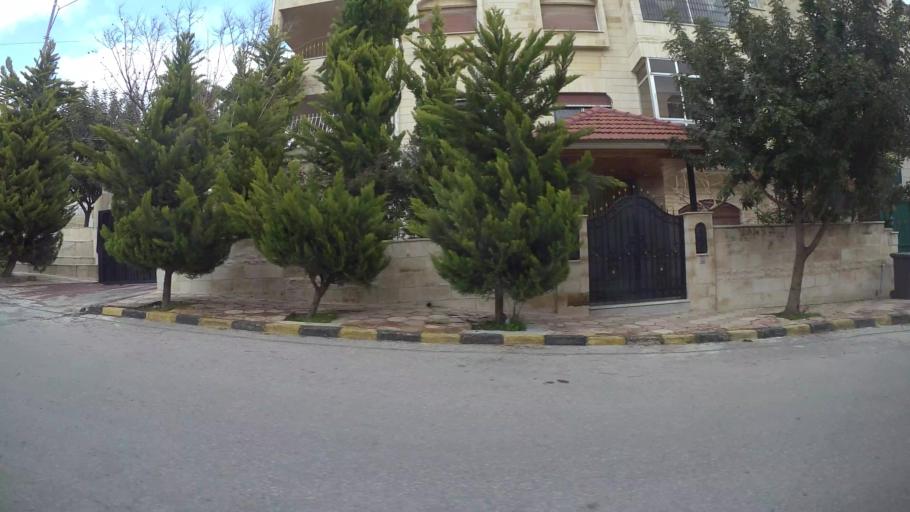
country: JO
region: Amman
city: Wadi as Sir
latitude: 31.9849
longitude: 35.8461
